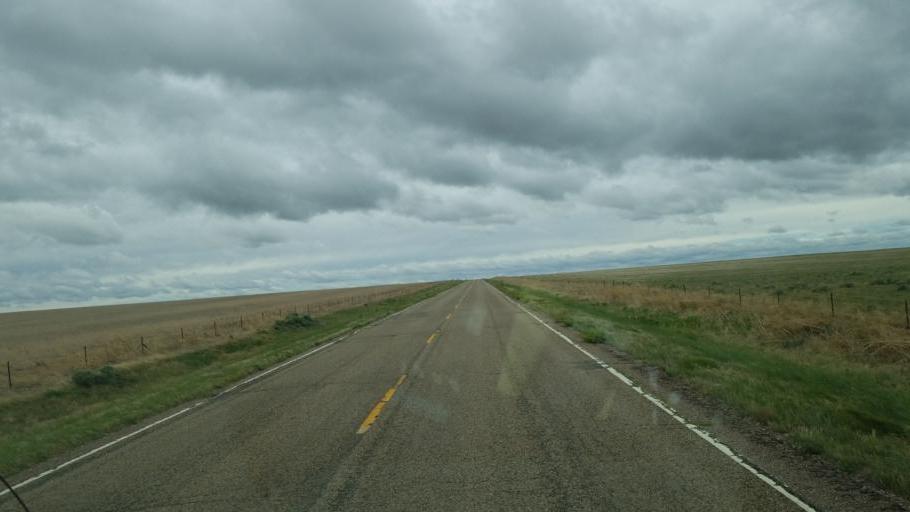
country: US
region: Colorado
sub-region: Lincoln County
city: Hugo
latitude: 38.8513
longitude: -103.6314
